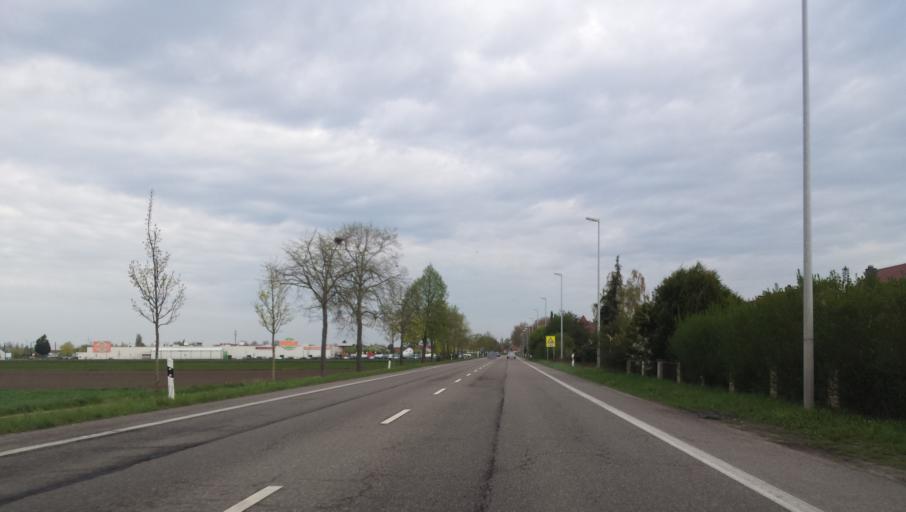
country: DE
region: Rheinland-Pfalz
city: Bobenheim-Roxheim
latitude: 49.5774
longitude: 8.3545
